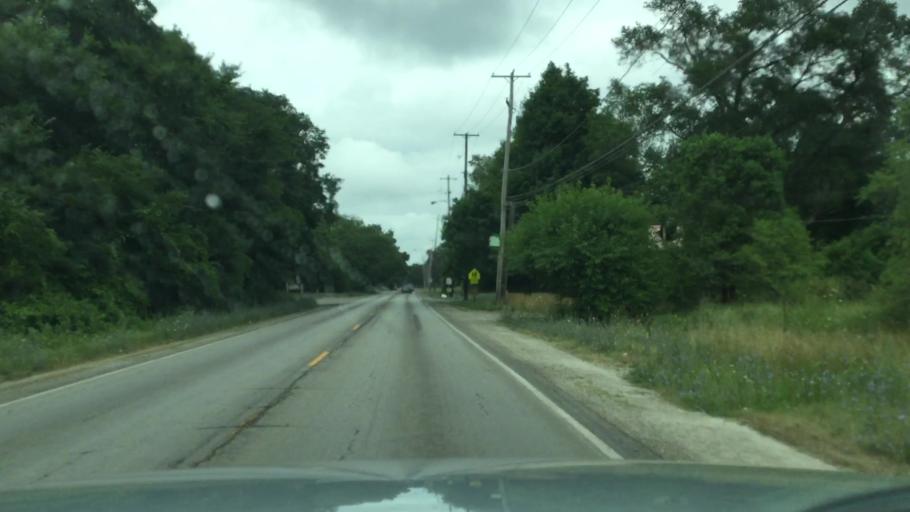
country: US
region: Michigan
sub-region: Genesee County
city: Beecher
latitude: 43.0759
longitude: -83.6701
